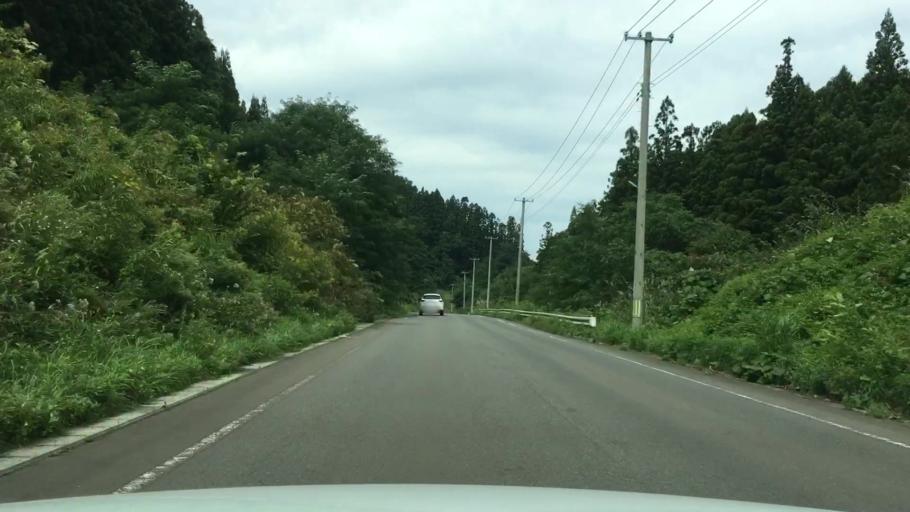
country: JP
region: Aomori
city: Shimokizukuri
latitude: 40.7424
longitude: 140.2438
